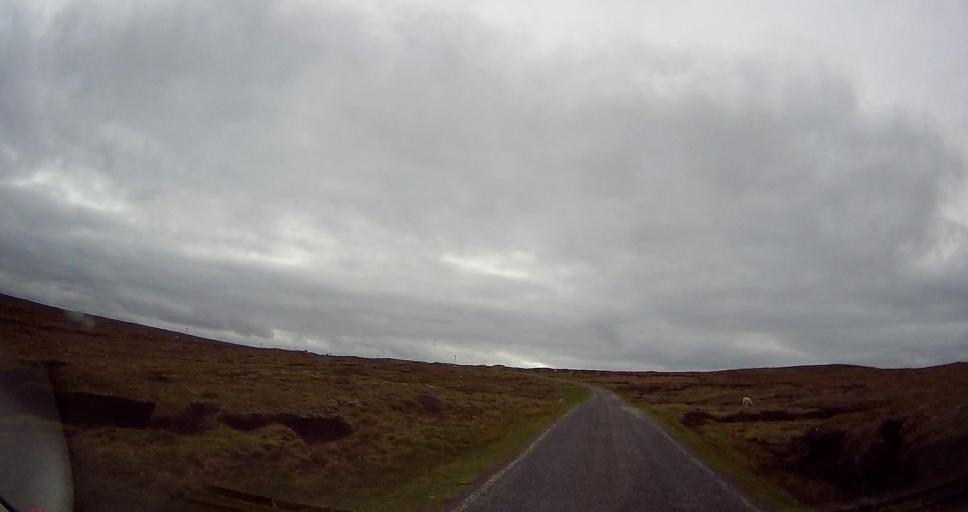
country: GB
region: Scotland
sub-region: Shetland Islands
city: Shetland
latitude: 60.5112
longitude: -1.1234
